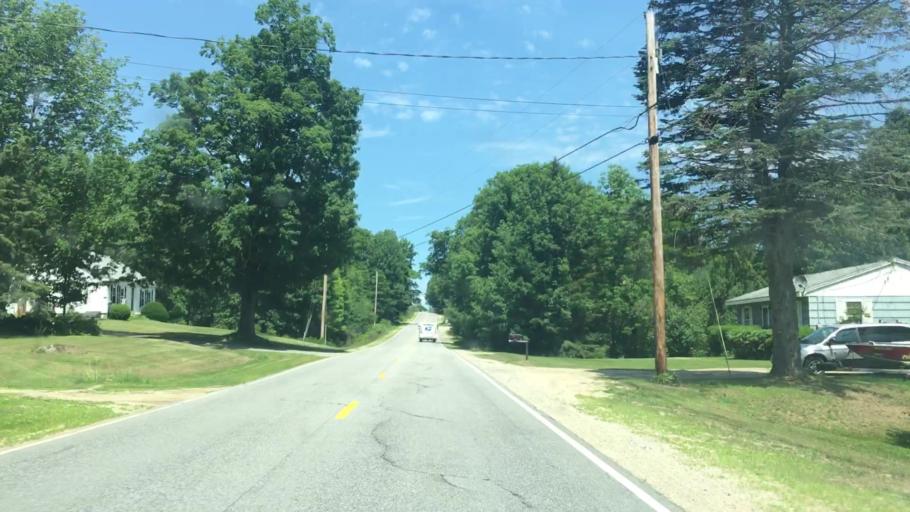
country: US
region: Maine
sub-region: Androscoggin County
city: Livermore
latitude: 44.3651
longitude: -70.2052
